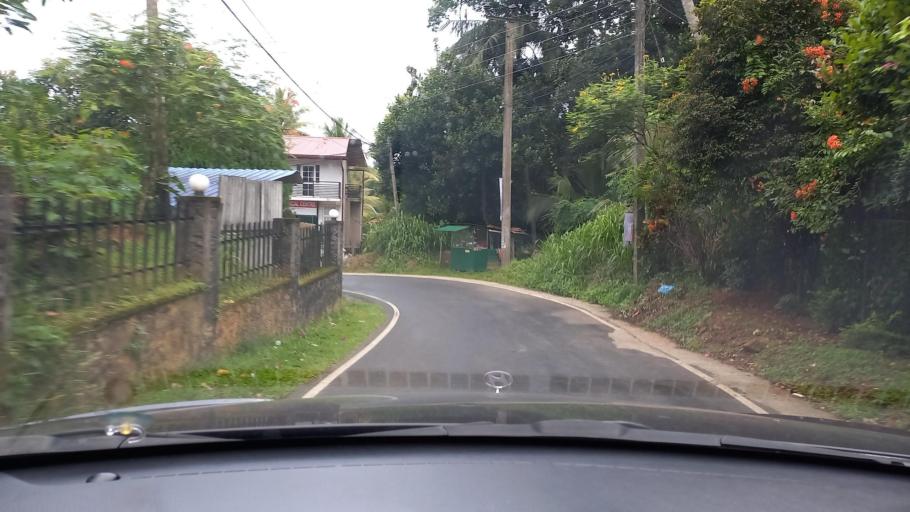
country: LK
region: Central
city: Kadugannawa
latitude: 7.2588
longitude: 80.3513
